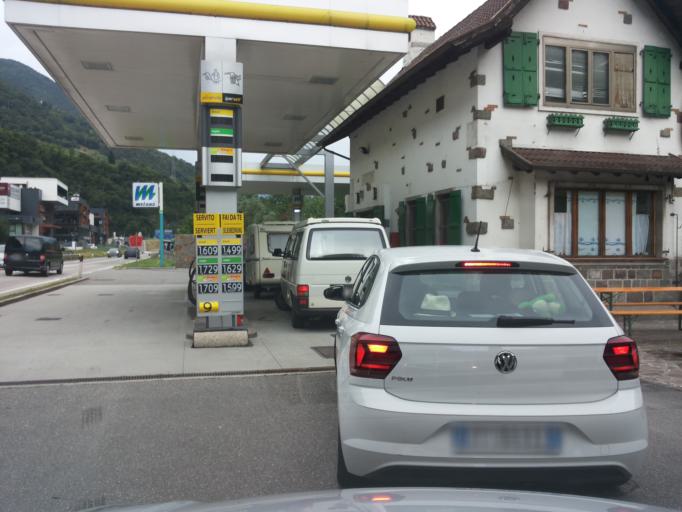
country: IT
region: Trentino-Alto Adige
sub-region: Bolzano
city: Cornedo All'Isarco
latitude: 46.4934
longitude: 11.4039
